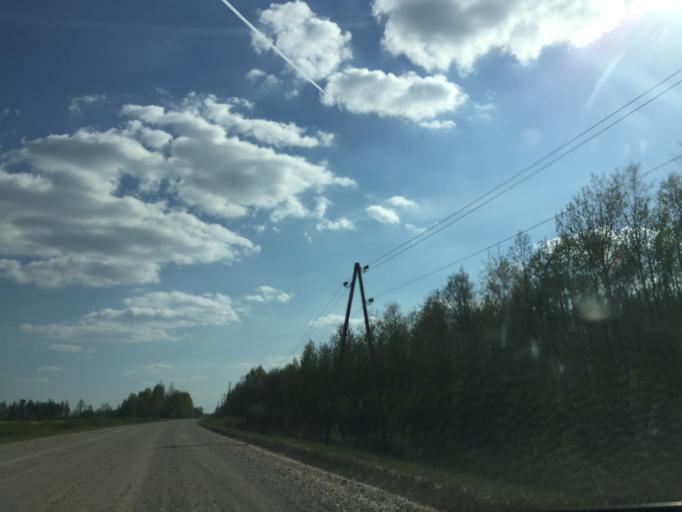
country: LV
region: Vecumnieki
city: Vecumnieki
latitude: 56.5317
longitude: 24.4185
